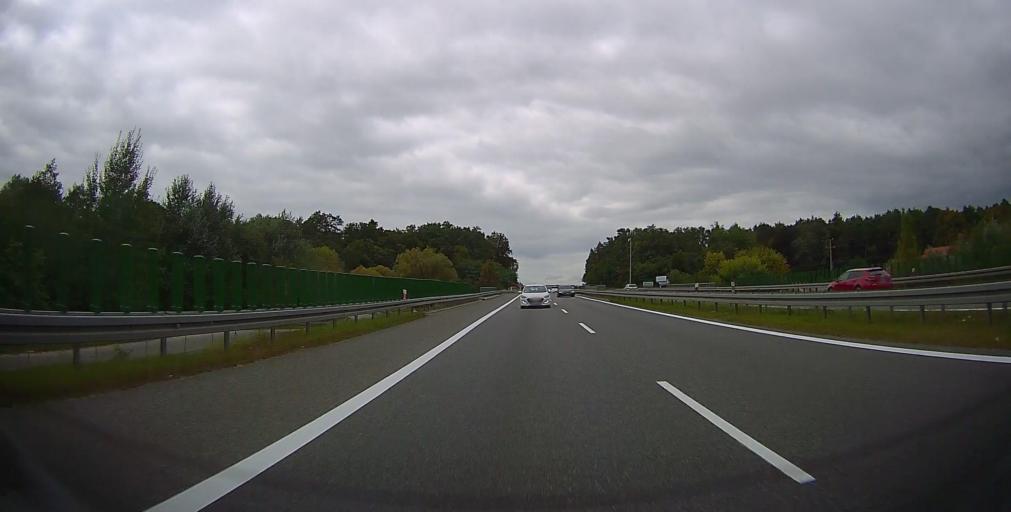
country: PL
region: Masovian Voivodeship
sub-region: Powiat grojecki
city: Grojec
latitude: 51.9048
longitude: 20.8581
